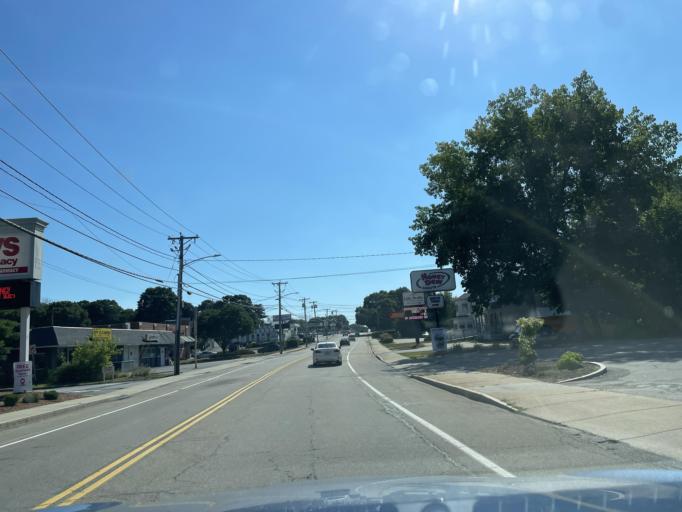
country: US
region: Massachusetts
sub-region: Worcester County
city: Webster
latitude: 42.0589
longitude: -71.8664
